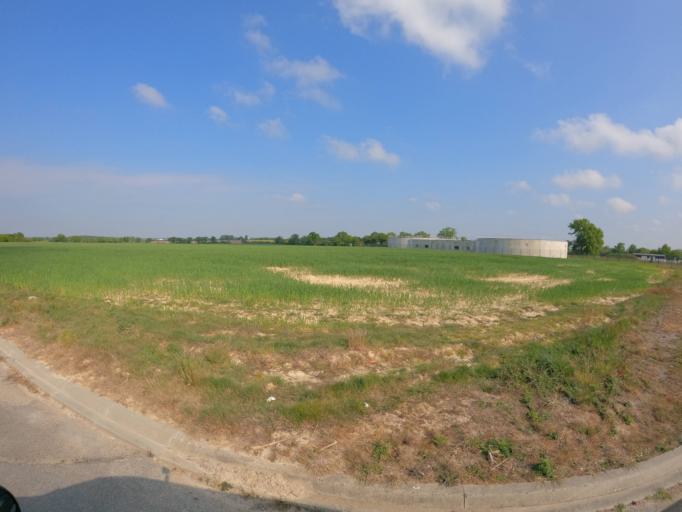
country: FR
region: Pays de la Loire
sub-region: Departement de la Vendee
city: La Bruffiere
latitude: 46.9982
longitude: -1.1709
